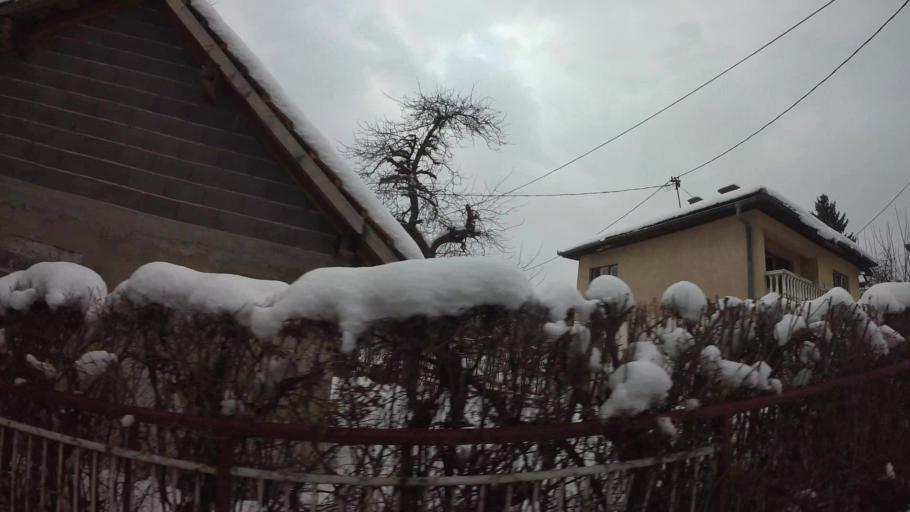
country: BA
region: Federation of Bosnia and Herzegovina
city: Kobilja Glava
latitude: 43.8610
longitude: 18.3878
